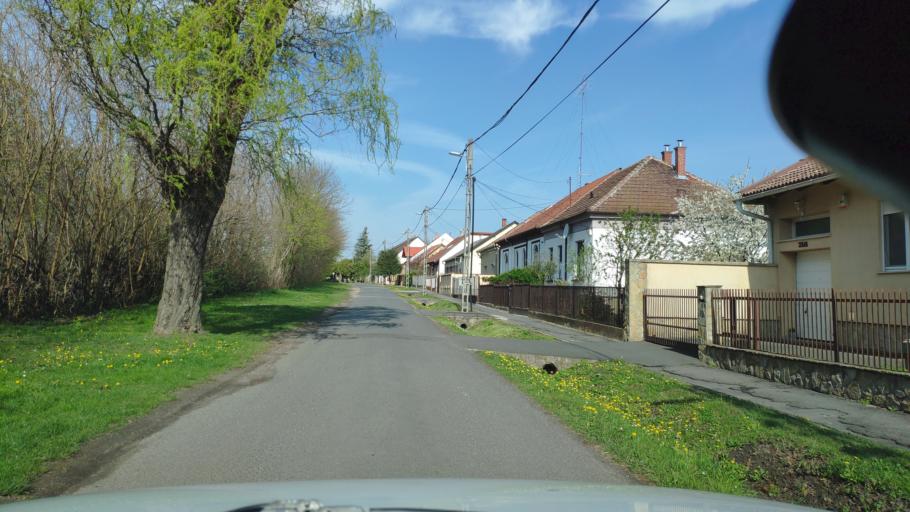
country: HU
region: Zala
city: Nagykanizsa
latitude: 46.4495
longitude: 17.0033
